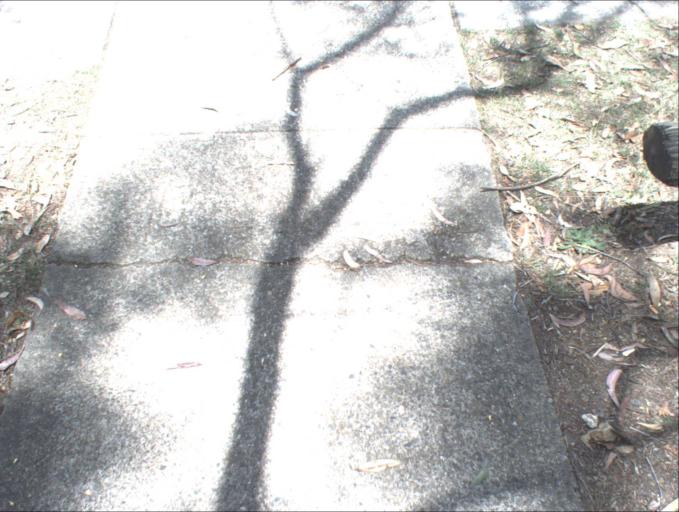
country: AU
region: Queensland
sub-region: Logan
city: Slacks Creek
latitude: -27.6549
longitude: 153.1693
